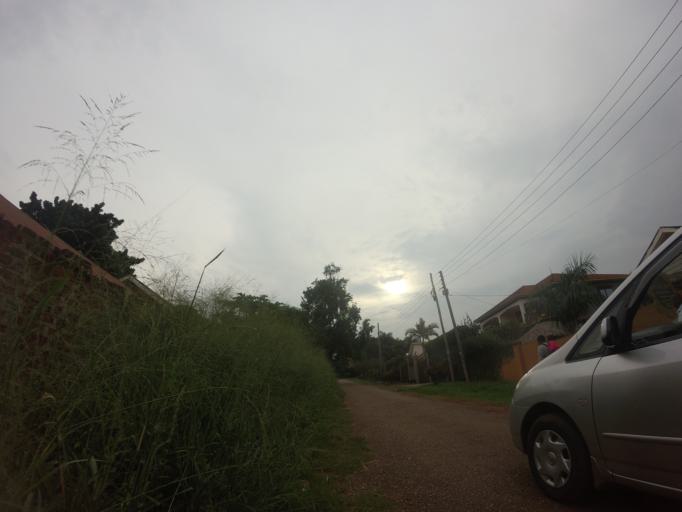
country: UG
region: Central Region
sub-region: Wakiso District
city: Kireka
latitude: 0.3481
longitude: 32.6206
